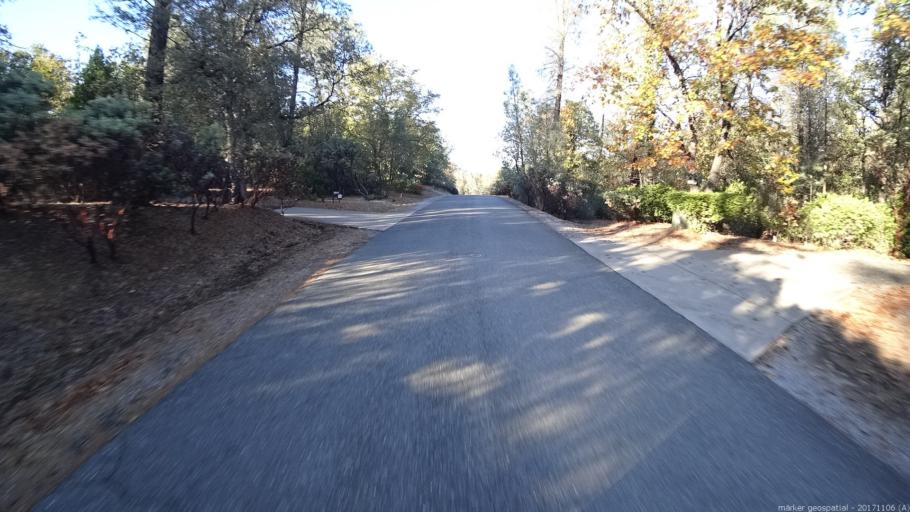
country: US
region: California
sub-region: Shasta County
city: Shasta
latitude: 40.5753
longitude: -122.4613
